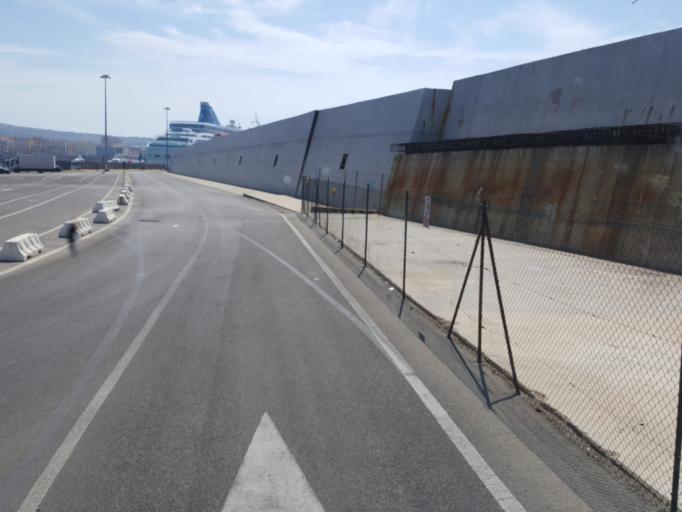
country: IT
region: Latium
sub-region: Citta metropolitana di Roma Capitale
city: Civitavecchia
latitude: 42.0934
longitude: 11.7795
